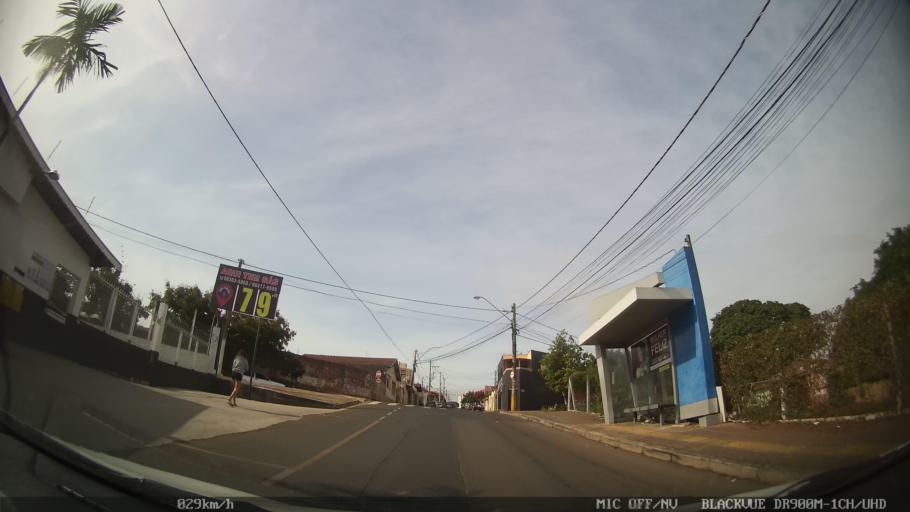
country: BR
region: Sao Paulo
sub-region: Piracicaba
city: Piracicaba
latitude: -22.7402
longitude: -47.6639
